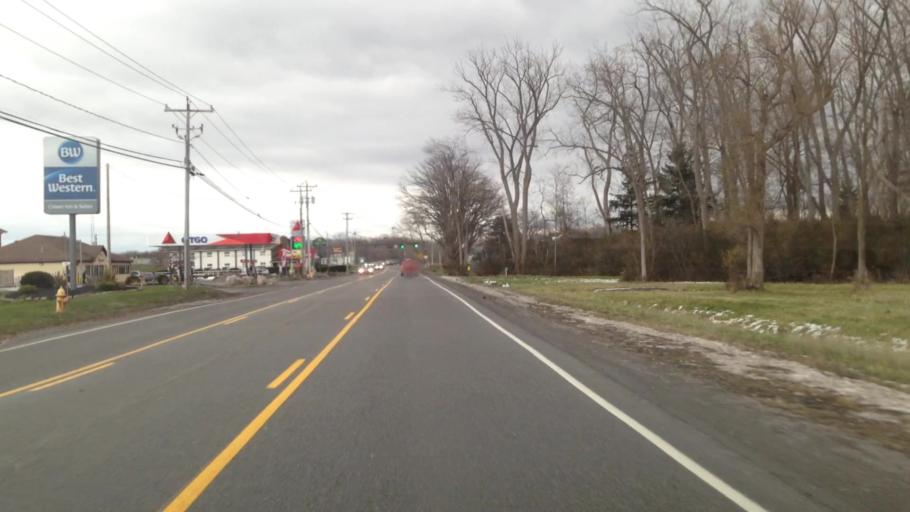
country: US
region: New York
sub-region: Genesee County
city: Batavia
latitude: 43.0165
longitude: -78.1956
